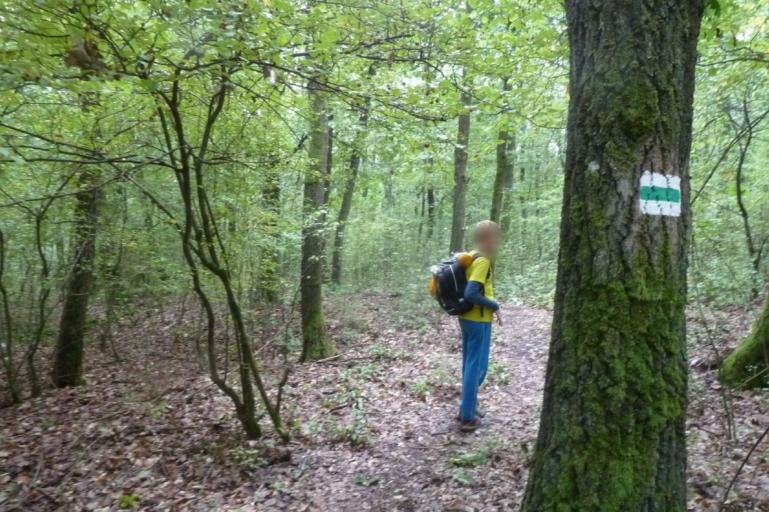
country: HU
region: Pest
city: Nagymaros
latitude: 47.8421
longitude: 18.9542
